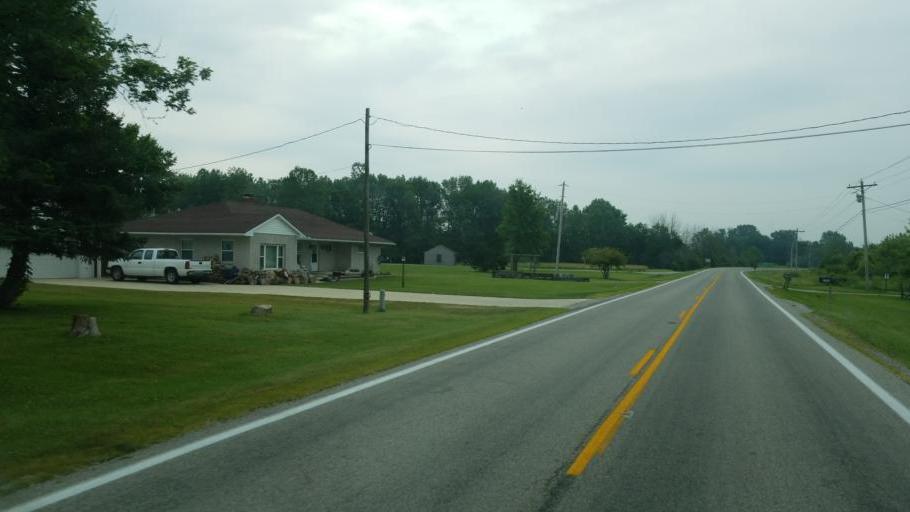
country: US
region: Ohio
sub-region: Union County
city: Richwood
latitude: 40.5763
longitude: -83.3393
